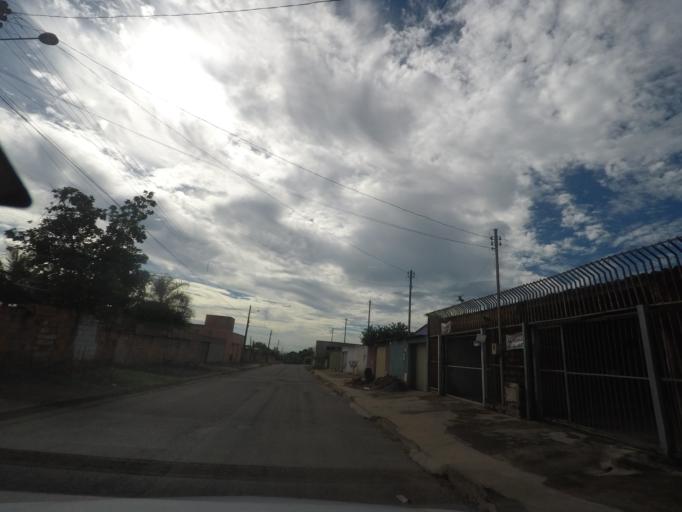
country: BR
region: Goias
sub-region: Aparecida De Goiania
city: Aparecida de Goiania
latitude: -16.8334
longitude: -49.2975
